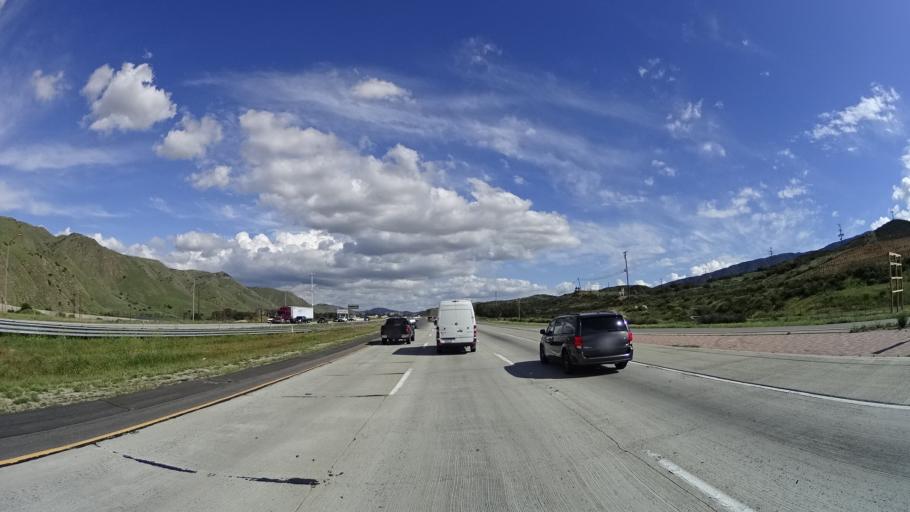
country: US
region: California
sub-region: Riverside County
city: El Cerrito
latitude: 33.7473
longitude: -117.4506
